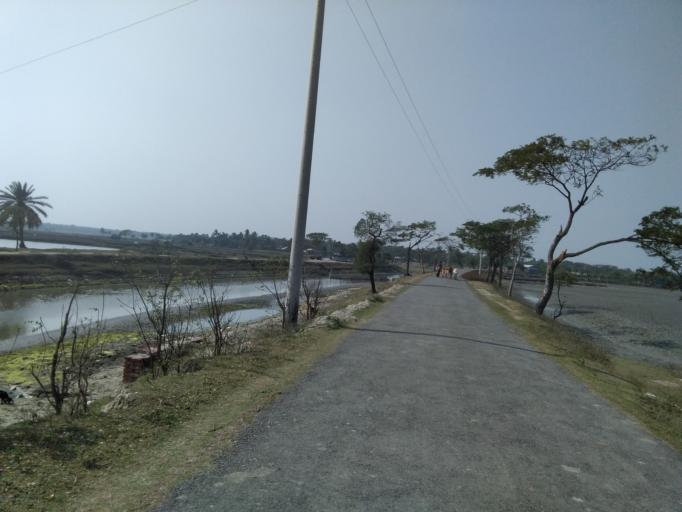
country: IN
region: West Bengal
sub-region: North 24 Parganas
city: Taki
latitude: 22.6359
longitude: 89.0052
